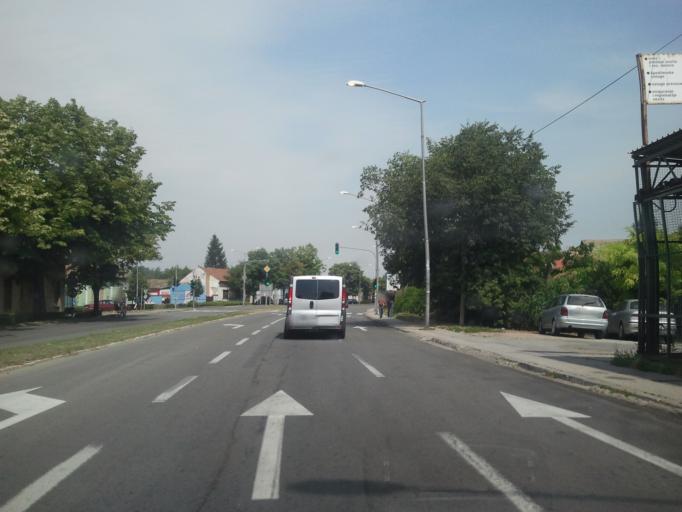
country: RS
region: Autonomna Pokrajina Vojvodina
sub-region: Juznobacki Okrug
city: Petrovaradin
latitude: 45.2420
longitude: 19.8829
